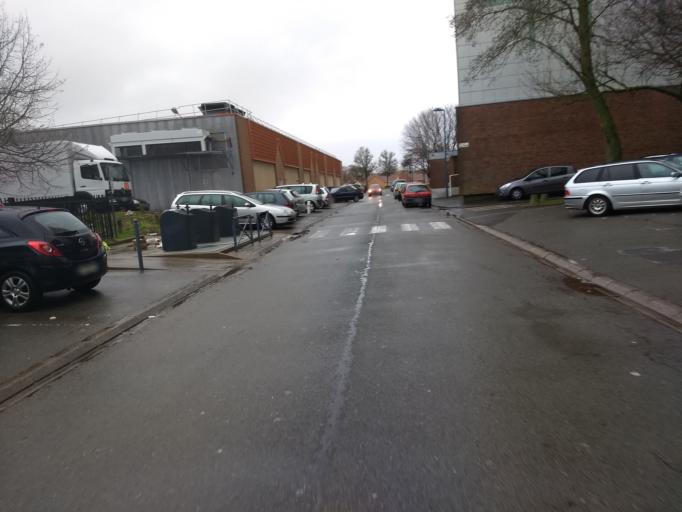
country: FR
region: Nord-Pas-de-Calais
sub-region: Departement du Pas-de-Calais
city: Arras
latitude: 50.2912
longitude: 2.7863
